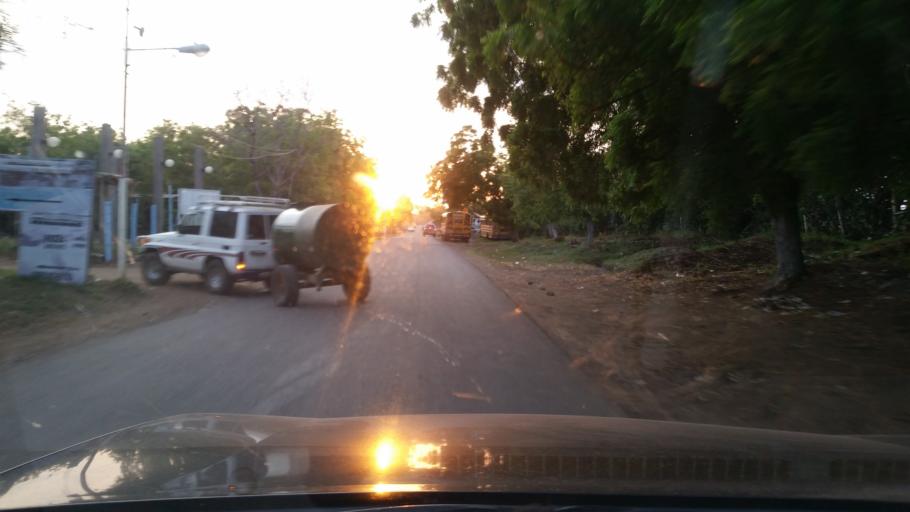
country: NI
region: Managua
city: Masachapa
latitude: 11.7782
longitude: -86.5106
